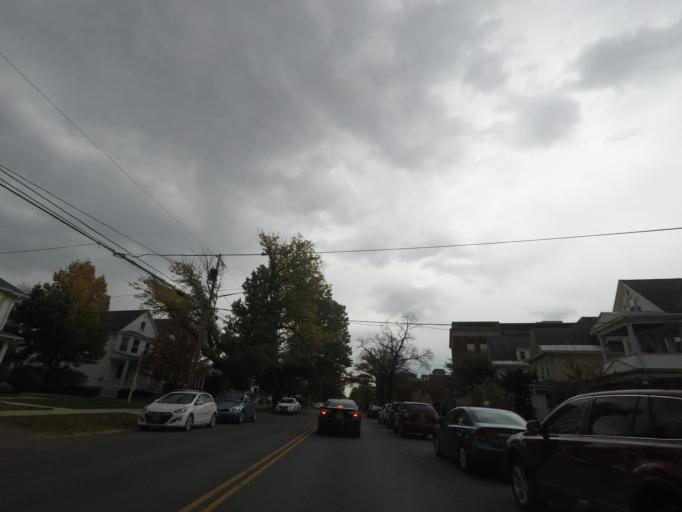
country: US
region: New York
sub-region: Albany County
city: West Albany
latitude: 42.6651
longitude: -73.7872
